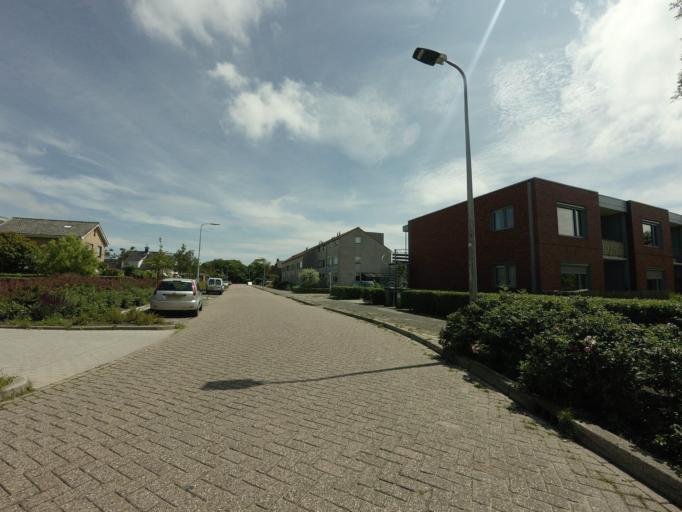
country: NL
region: North Holland
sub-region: Gemeente Texel
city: Den Burg
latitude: 53.0857
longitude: 4.8726
